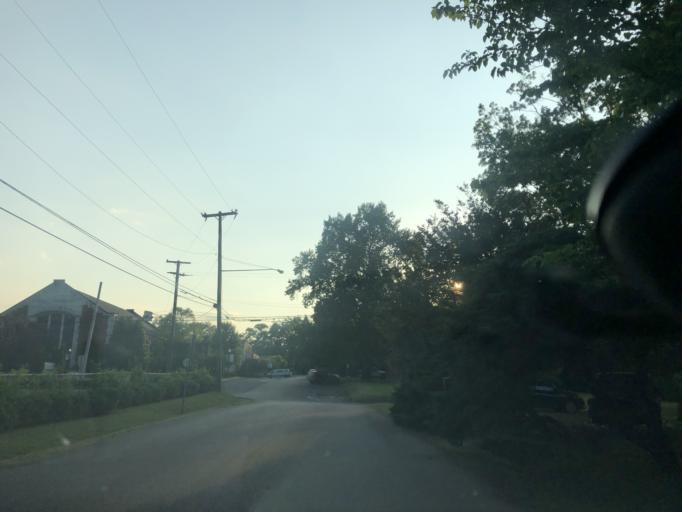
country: US
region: Tennessee
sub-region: Davidson County
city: Oak Hill
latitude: 36.1077
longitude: -86.7934
